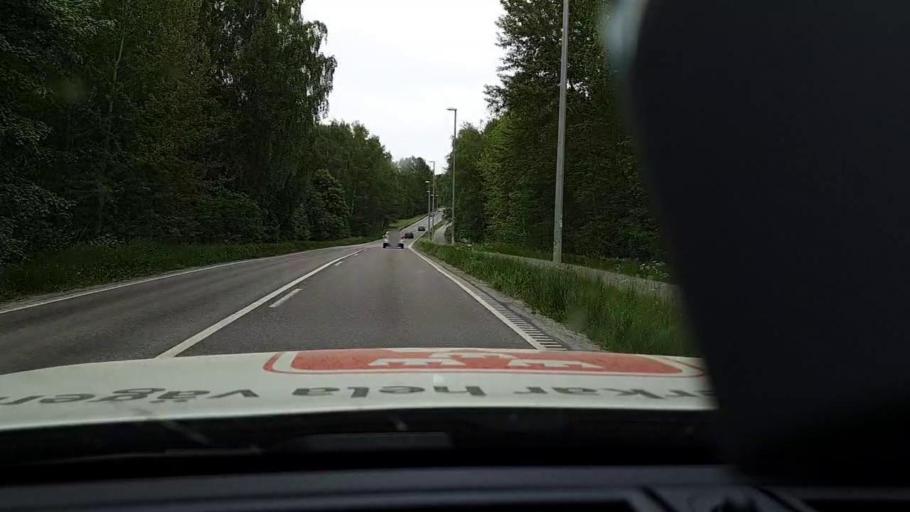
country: SE
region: Stockholm
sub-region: Tyreso Kommun
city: Bollmora
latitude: 59.2011
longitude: 18.1921
